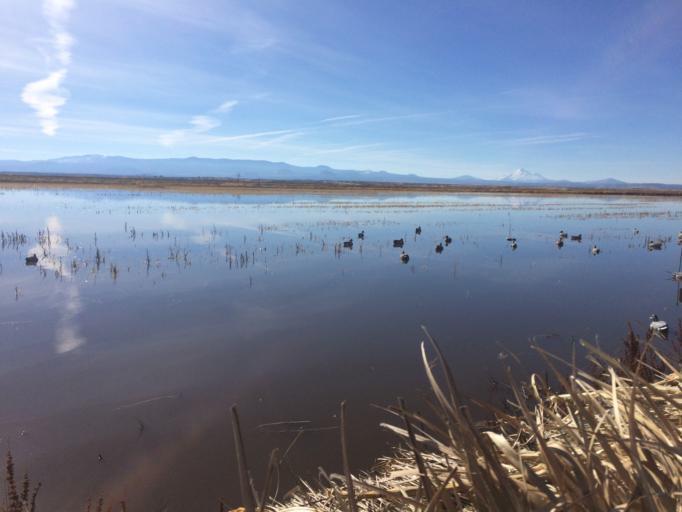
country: US
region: California
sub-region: Siskiyou County
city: Tulelake
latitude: 41.8511
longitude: -121.4262
